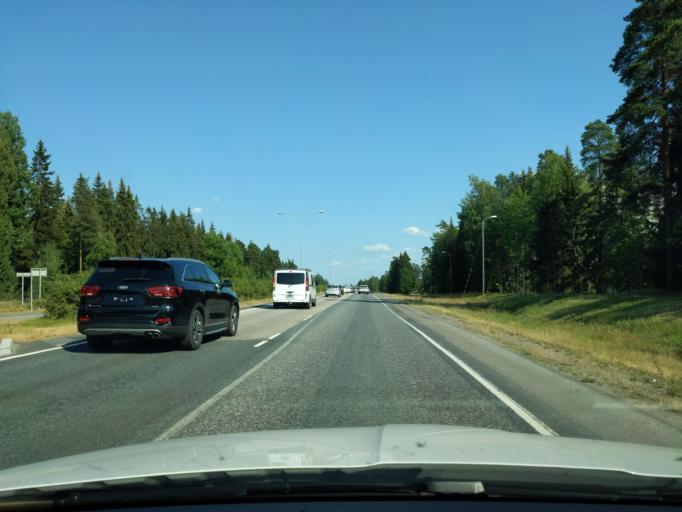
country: FI
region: Paijanne Tavastia
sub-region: Lahti
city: Lahti
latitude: 60.9808
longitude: 25.5974
